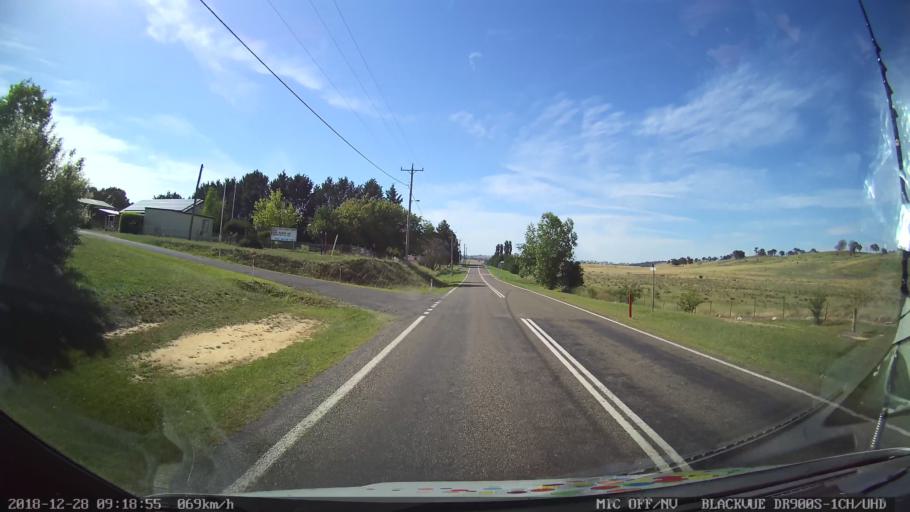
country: AU
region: New South Wales
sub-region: Upper Lachlan Shire
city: Crookwell
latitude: -34.3311
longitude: 149.3662
